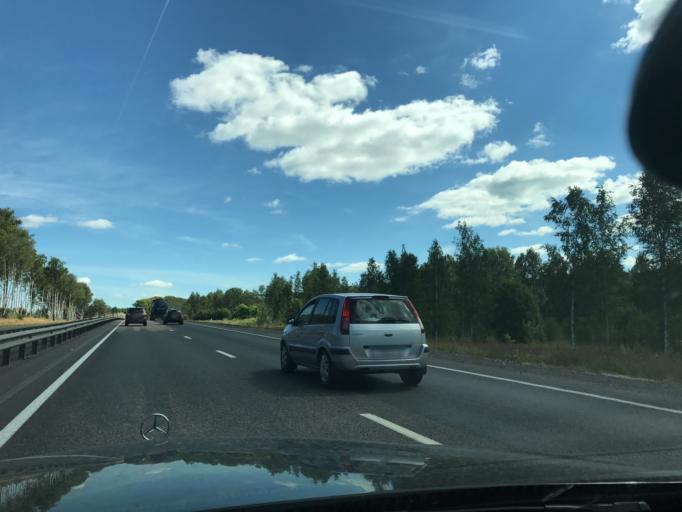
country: RU
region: Vladimir
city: Gorokhovets
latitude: 56.1655
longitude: 42.4825
